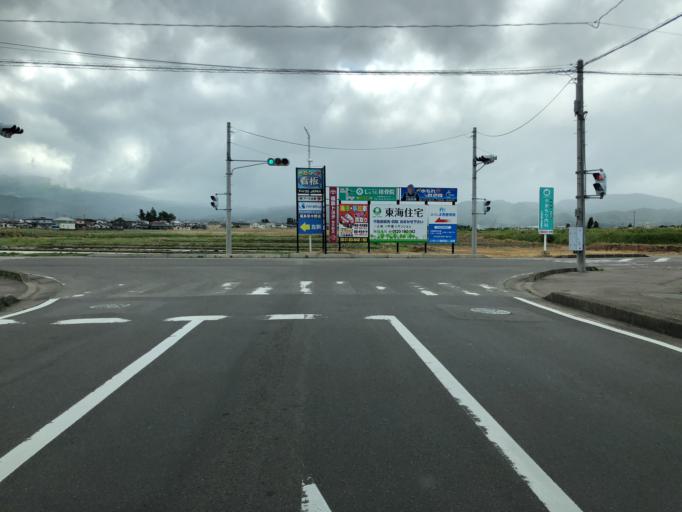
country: JP
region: Fukushima
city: Fukushima-shi
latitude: 37.7710
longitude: 140.4347
